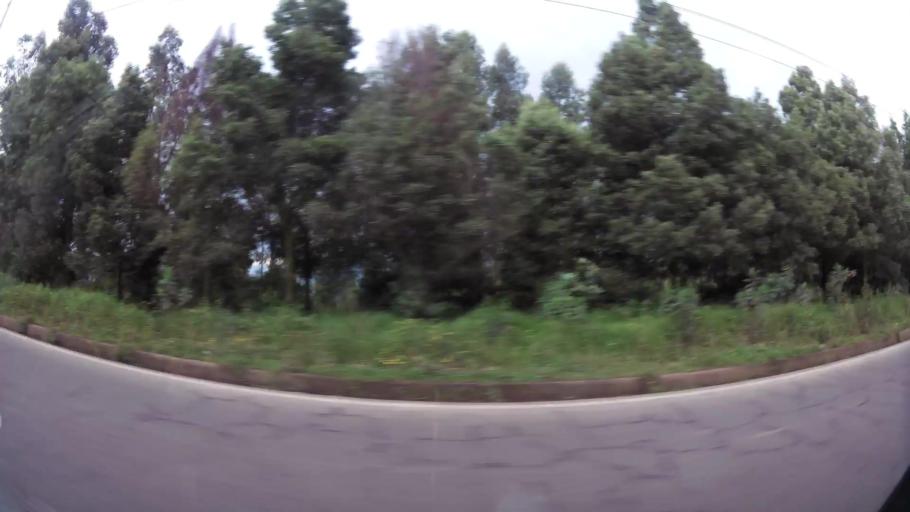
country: EC
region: Pichincha
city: Sangolqui
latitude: -0.3245
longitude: -78.5196
